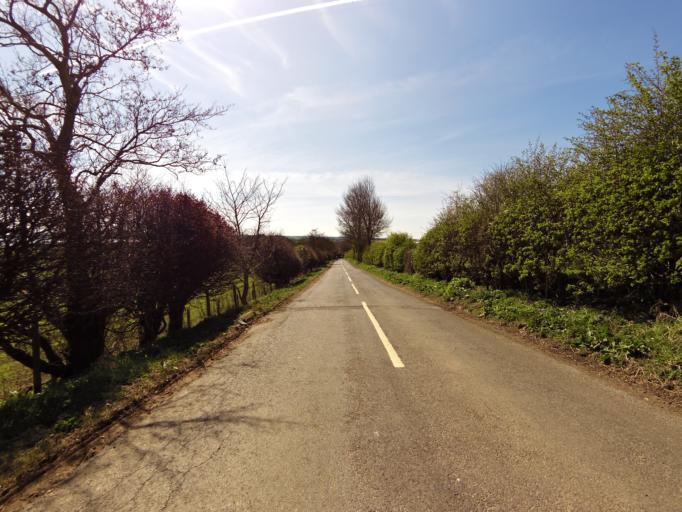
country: GB
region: Scotland
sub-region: Angus
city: Montrose
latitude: 56.6591
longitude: -2.5106
